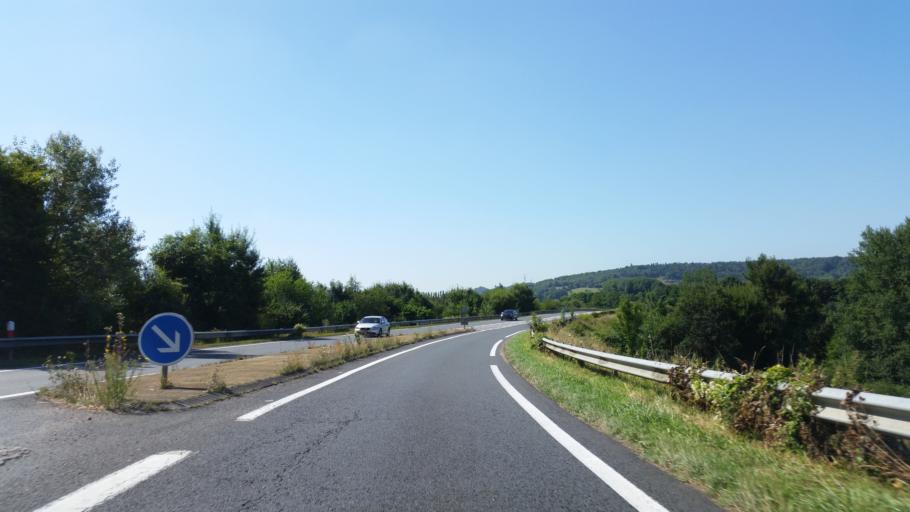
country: FR
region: Lower Normandy
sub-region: Departement du Calvados
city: Lisieux
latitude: 49.2375
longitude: 0.2222
